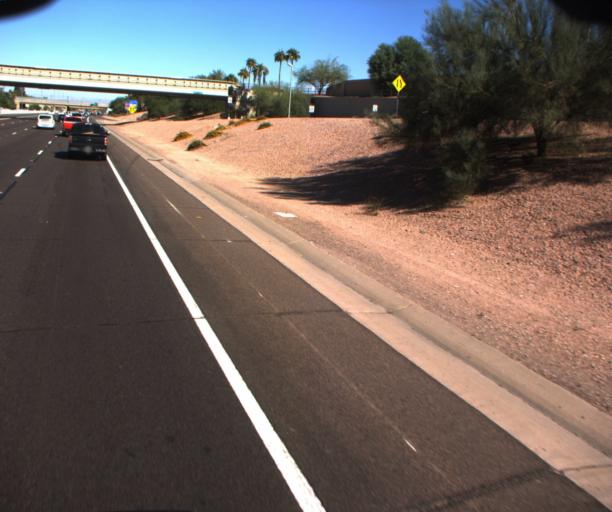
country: US
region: Arizona
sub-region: Maricopa County
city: Tempe
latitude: 33.4100
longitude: -111.8911
